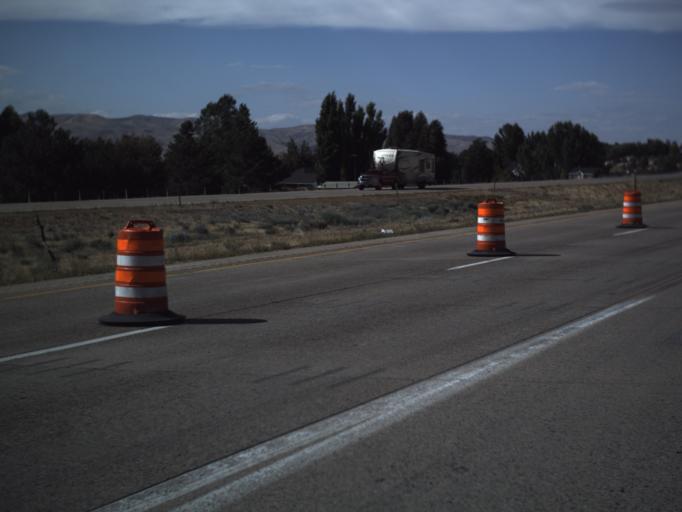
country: US
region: Utah
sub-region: Juab County
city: Nephi
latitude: 39.7152
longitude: -111.8168
